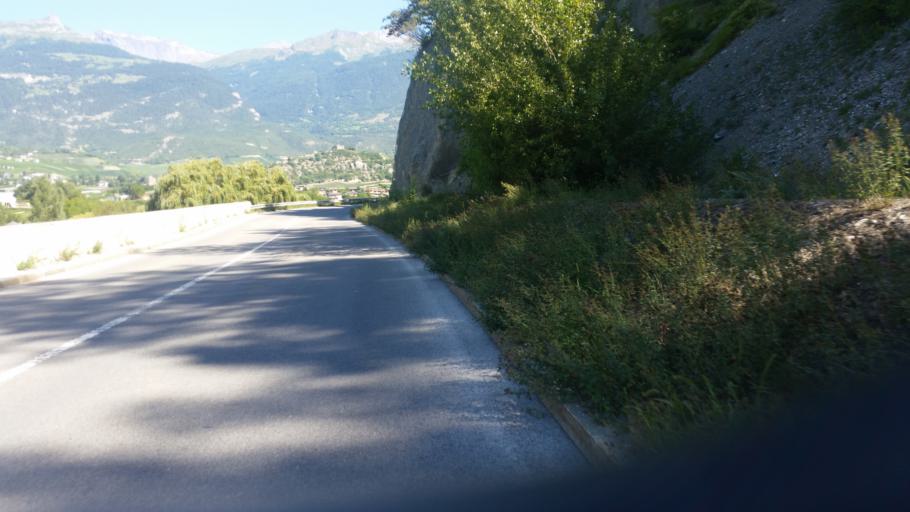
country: CH
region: Valais
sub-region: Sierre District
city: Chippis
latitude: 46.2860
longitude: 7.5424
